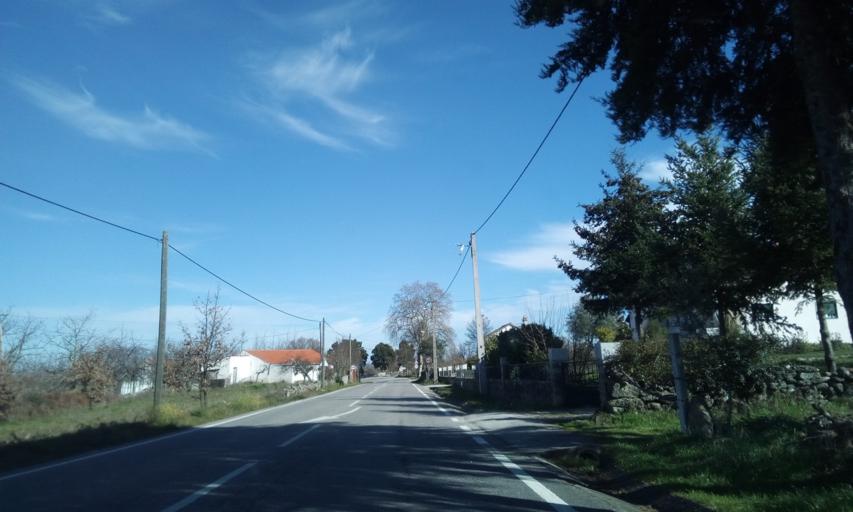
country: PT
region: Guarda
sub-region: Guarda
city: Sequeira
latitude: 40.5958
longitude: -7.1253
